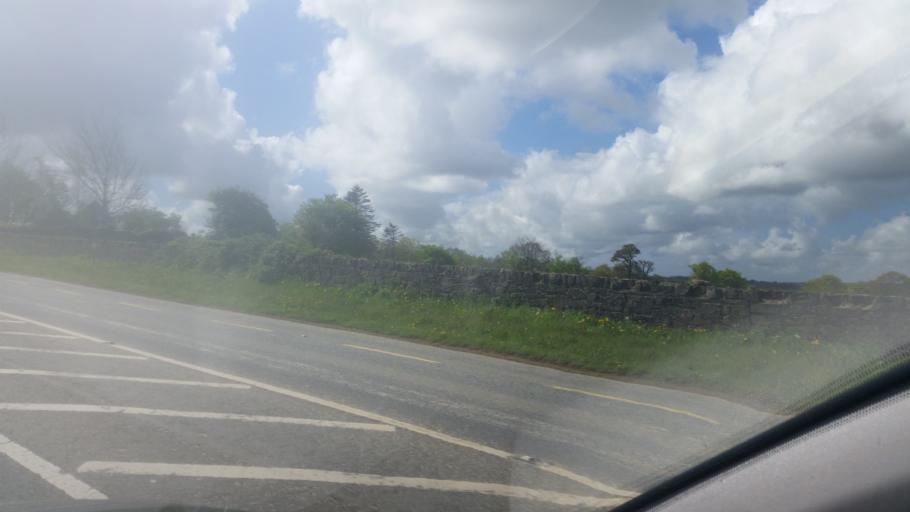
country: IE
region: Leinster
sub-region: Loch Garman
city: Enniscorthy
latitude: 52.4512
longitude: -6.5510
